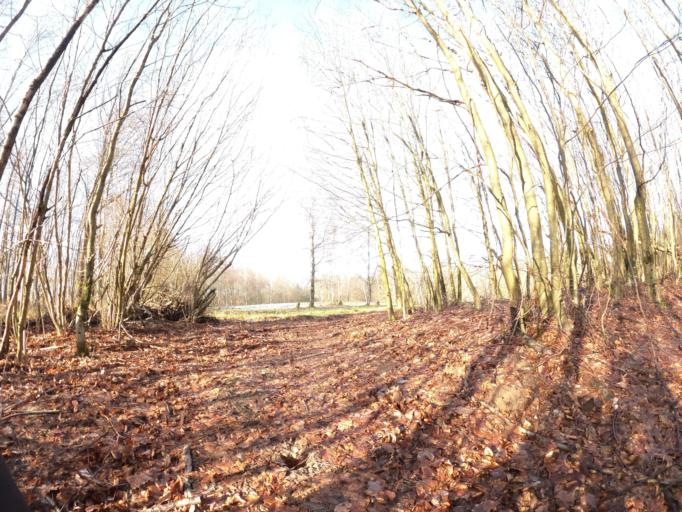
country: PL
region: West Pomeranian Voivodeship
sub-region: Powiat koszalinski
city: Polanow
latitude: 54.1336
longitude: 16.7749
